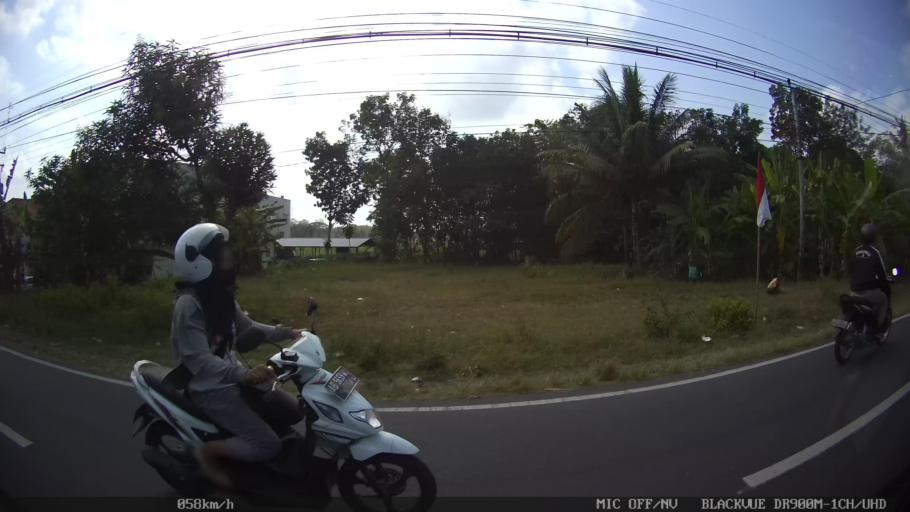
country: ID
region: Daerah Istimewa Yogyakarta
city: Srandakan
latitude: -7.8489
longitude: 110.2183
